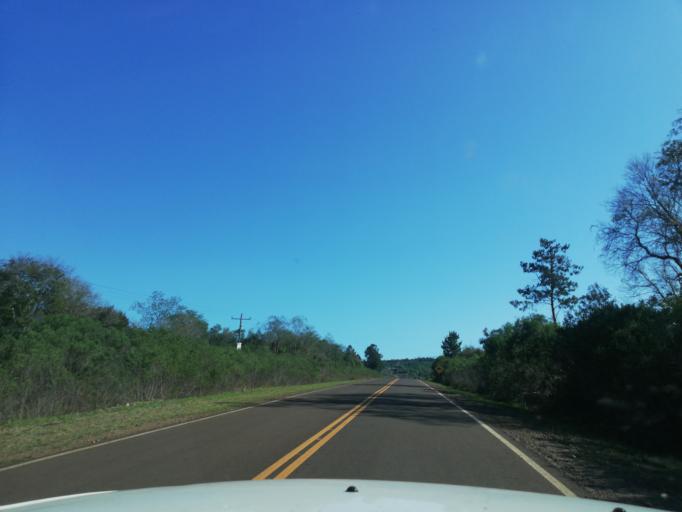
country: AR
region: Misiones
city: Arroyo del Medio
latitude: -27.6877
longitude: -55.3974
